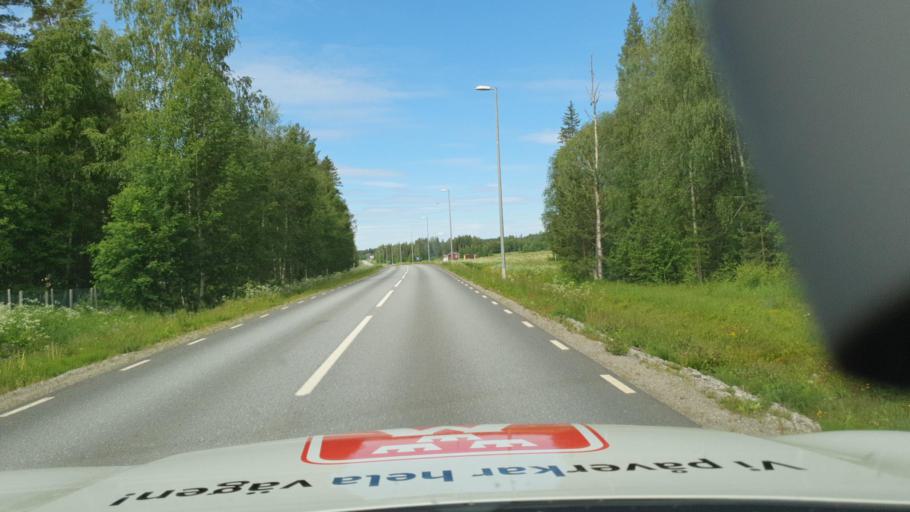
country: SE
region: Vaesterbotten
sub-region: Skelleftea Kommun
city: Forsbacka
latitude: 64.6933
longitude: 20.4957
